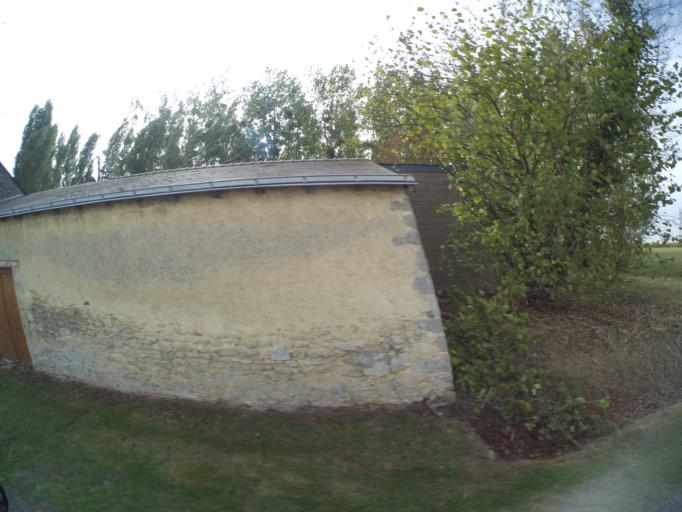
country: FR
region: Pays de la Loire
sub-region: Departement de Maine-et-Loire
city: Martigne-Briand
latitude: 47.2066
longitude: -0.4639
